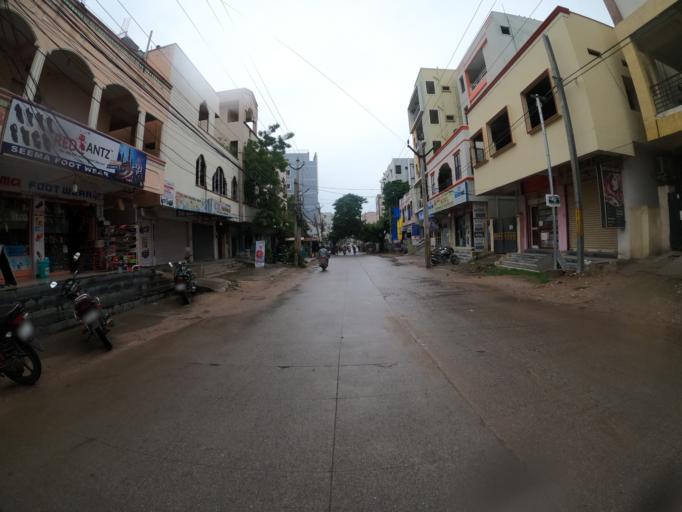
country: IN
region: Telangana
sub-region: Rangareddi
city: Kukatpalli
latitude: 17.4582
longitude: 78.4033
